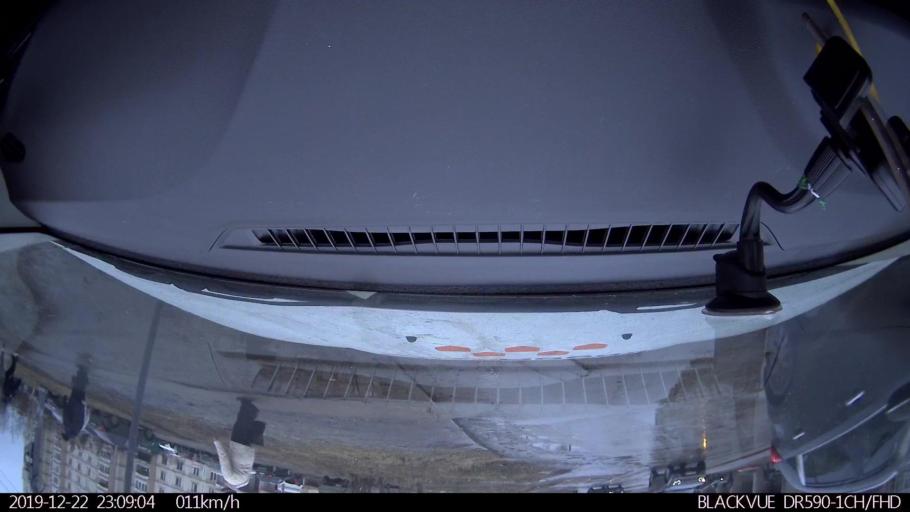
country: RU
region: Nizjnij Novgorod
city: Gorbatovka
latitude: 56.2607
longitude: 43.8514
